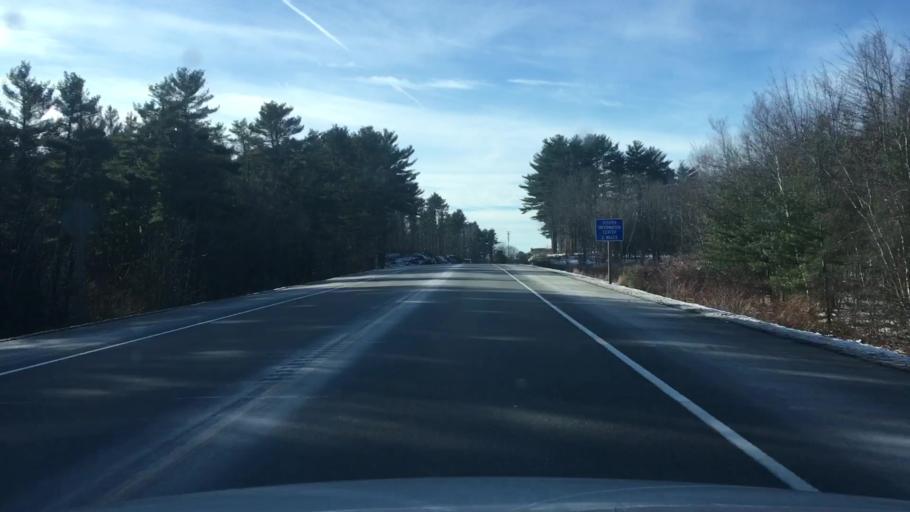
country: US
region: Maine
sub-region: Sagadahoc County
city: Woolwich
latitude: 43.9290
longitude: -69.7866
